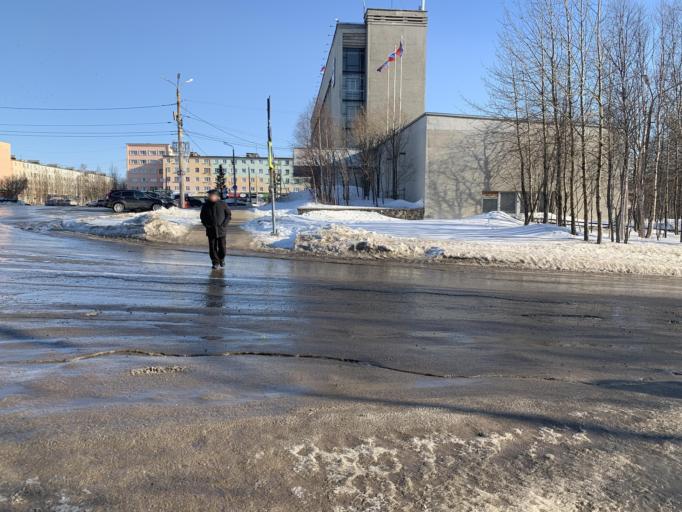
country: RU
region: Murmansk
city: Monchegorsk
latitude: 67.9383
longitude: 32.9358
